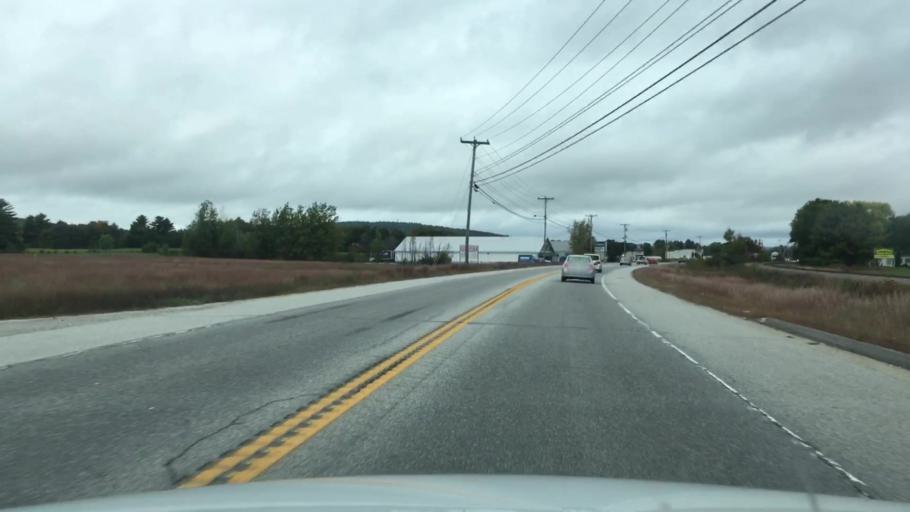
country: US
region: Maine
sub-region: Oxford County
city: South Paris
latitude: 44.1764
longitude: -70.5138
